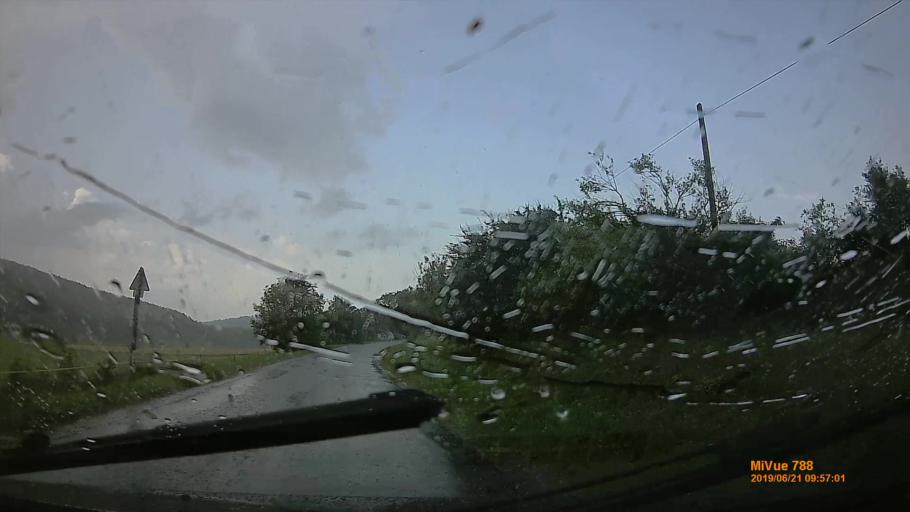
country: HU
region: Baranya
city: Buekkoesd
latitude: 46.2227
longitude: 17.9759
